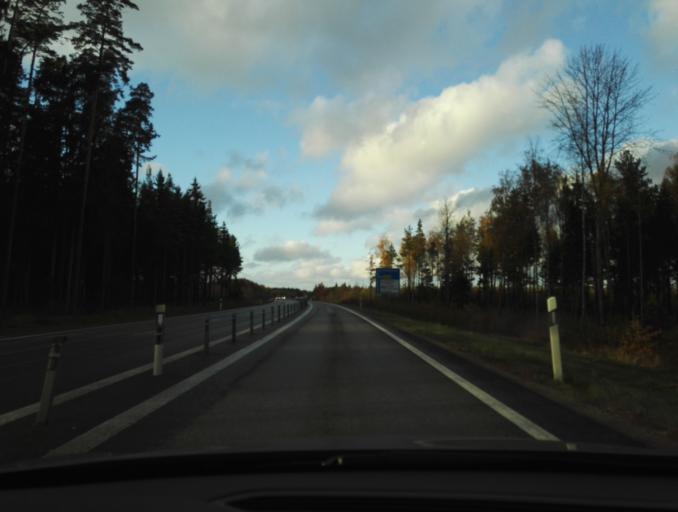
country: SE
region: Kronoberg
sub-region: Vaxjo Kommun
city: Vaexjoe
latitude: 56.9065
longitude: 14.7271
